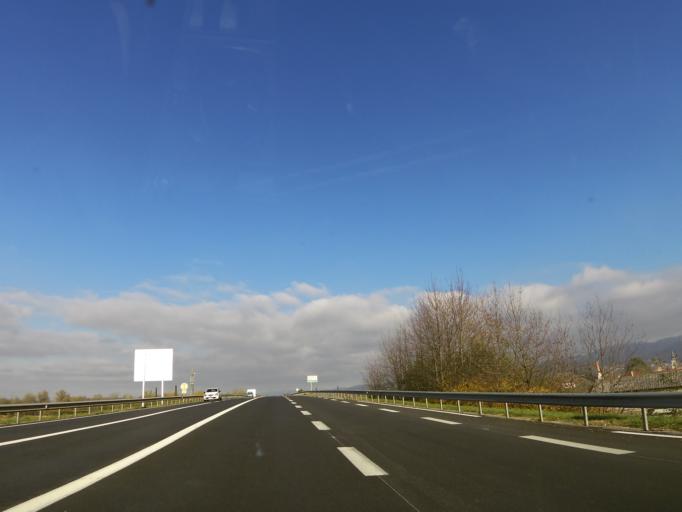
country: FR
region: Rhone-Alpes
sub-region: Departement de l'Ain
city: Saint-Denis-en-Bugey
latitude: 45.9493
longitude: 5.3208
